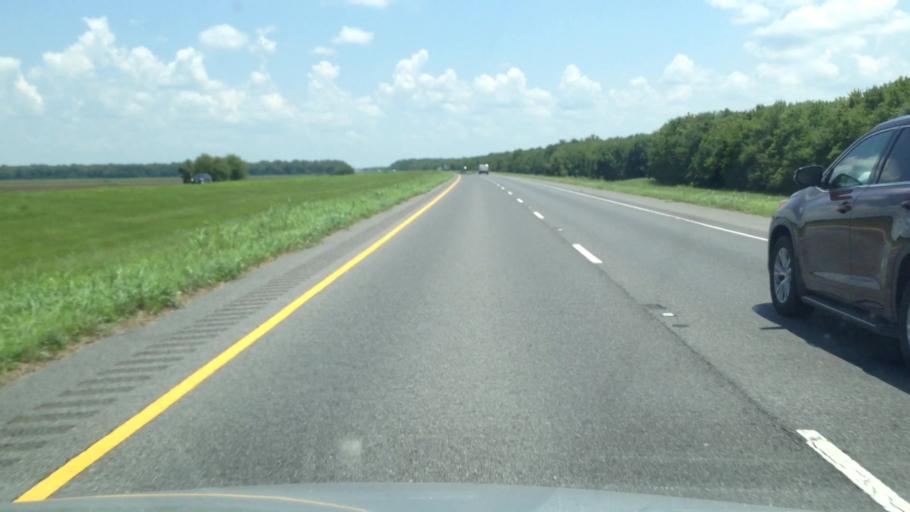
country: US
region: Louisiana
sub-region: Evangeline Parish
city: Ville Platte
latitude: 30.8074
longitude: -92.2154
